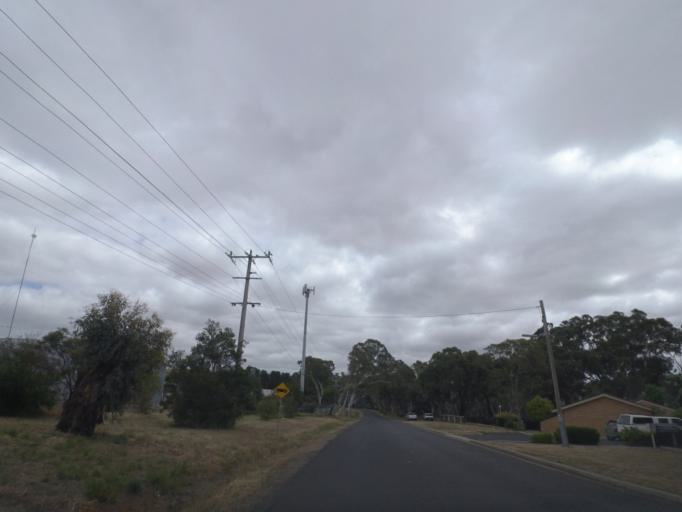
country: AU
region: Victoria
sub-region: Whittlesea
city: Whittlesea
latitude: -37.2015
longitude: 145.0418
